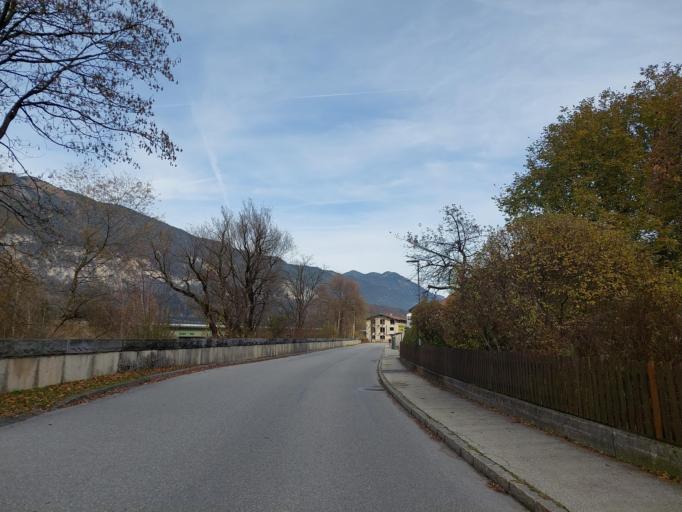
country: AT
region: Tyrol
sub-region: Politischer Bezirk Kufstein
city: Rattenberg
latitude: 47.4418
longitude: 11.8947
